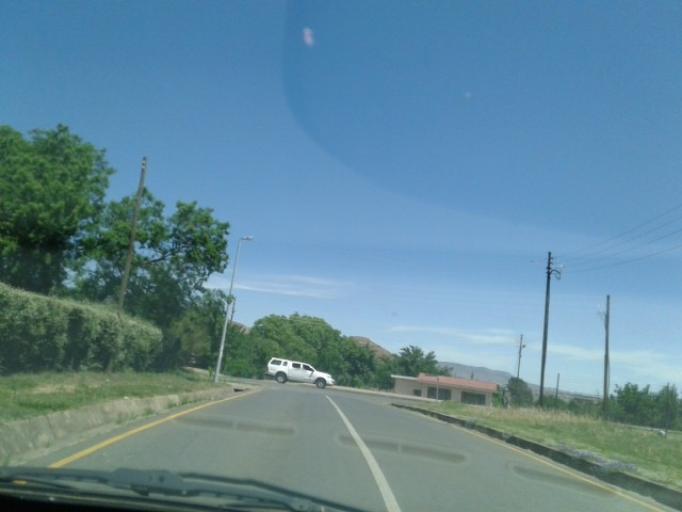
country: LS
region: Maseru
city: Maseru
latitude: -29.3057
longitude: 27.4726
